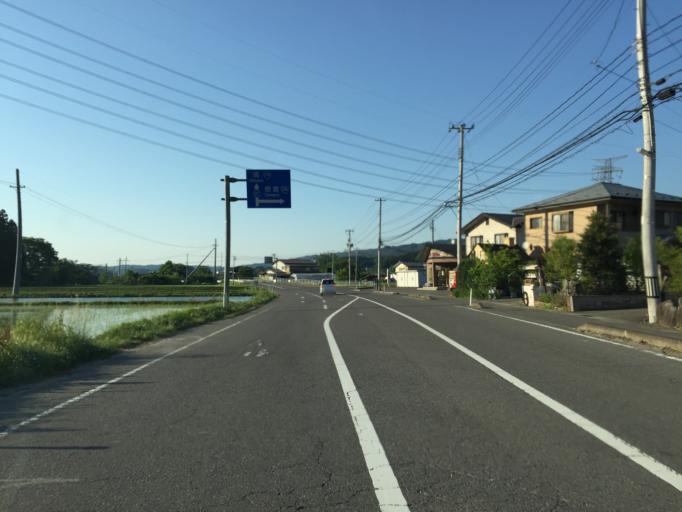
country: JP
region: Ibaraki
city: Daigo
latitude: 36.9446
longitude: 140.4403
